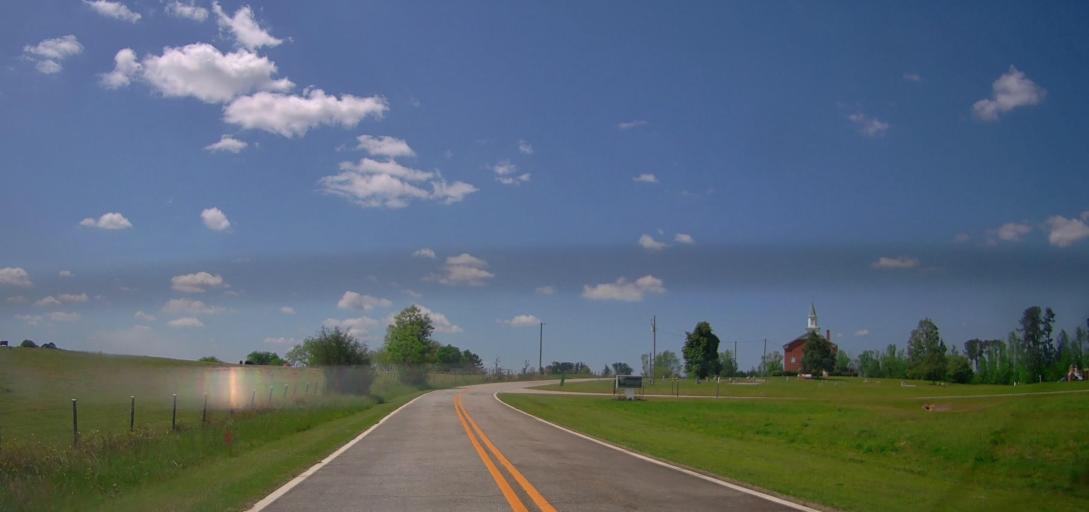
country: US
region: Georgia
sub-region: Putnam County
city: Eatonton
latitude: 33.3365
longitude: -83.3253
